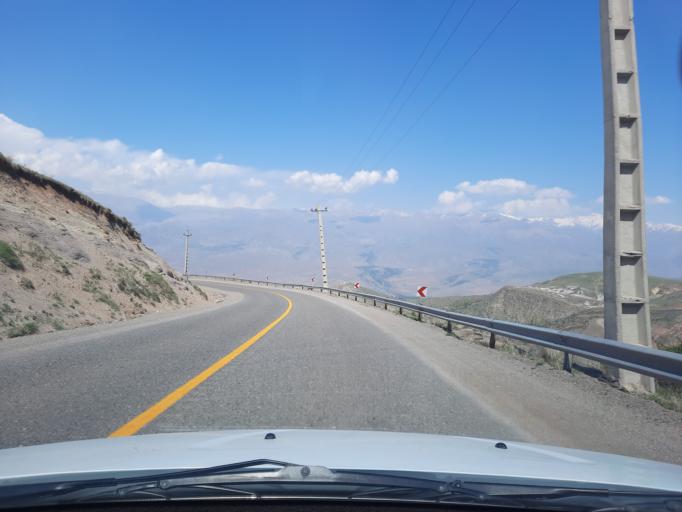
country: IR
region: Qazvin
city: Qazvin
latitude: 36.4032
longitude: 50.2221
